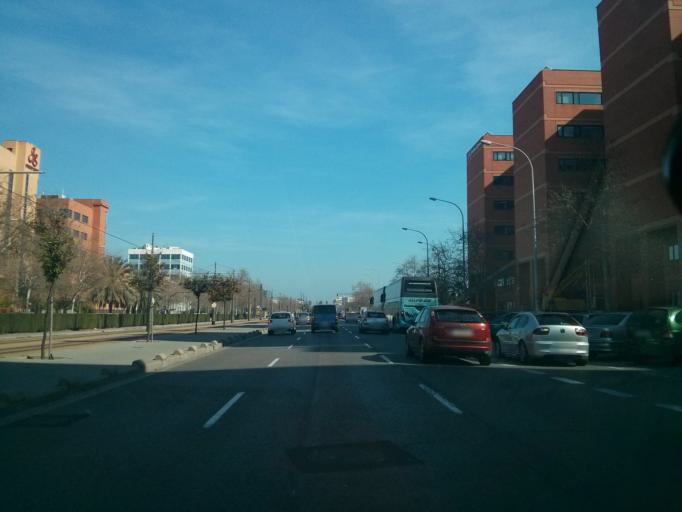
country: ES
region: Valencia
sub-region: Provincia de Valencia
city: Alboraya
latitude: 39.4787
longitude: -0.3419
